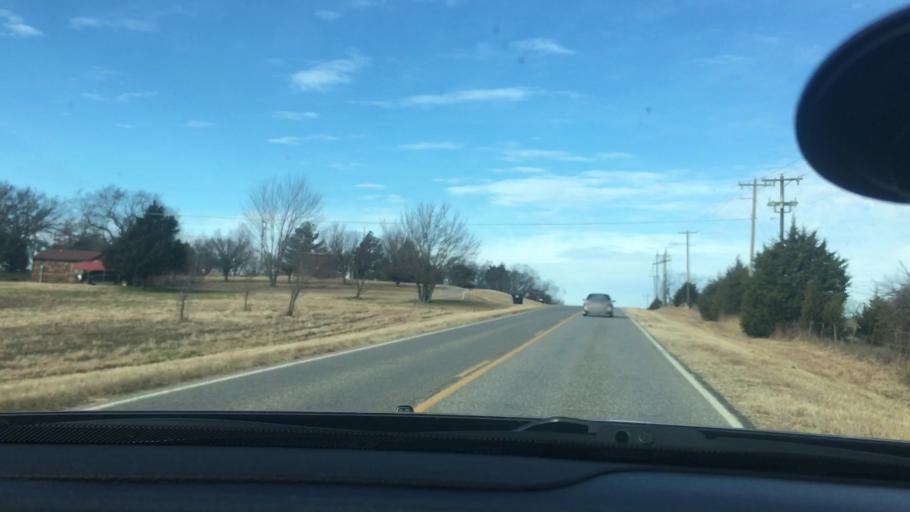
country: US
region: Oklahoma
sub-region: Seminole County
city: Konawa
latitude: 34.9471
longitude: -96.7330
